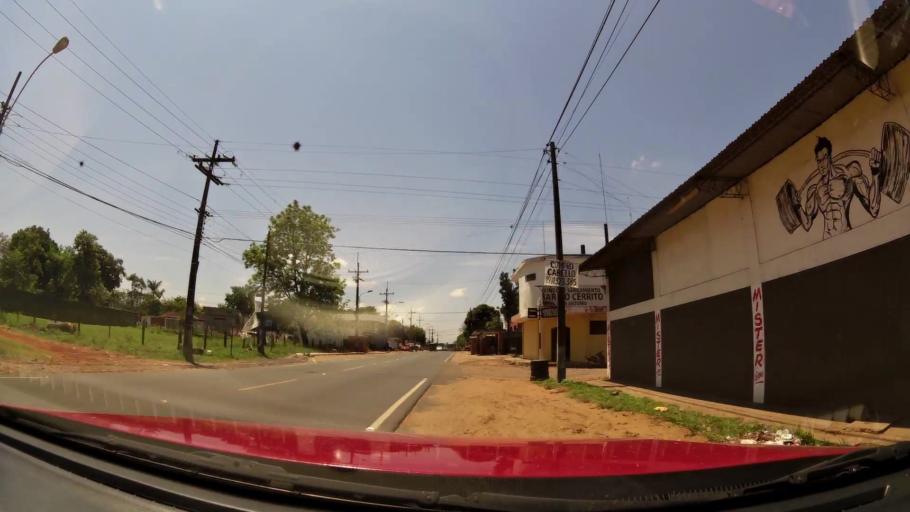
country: PY
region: Central
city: San Antonio
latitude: -25.4115
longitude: -57.5495
